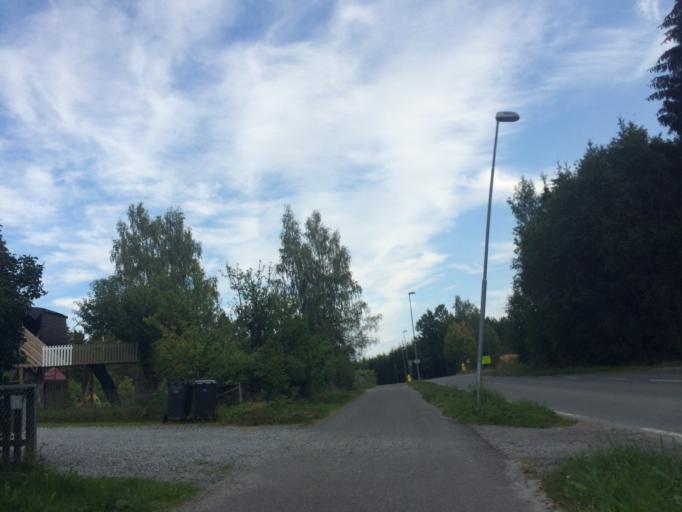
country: NO
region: Akershus
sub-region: Ski
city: Ski
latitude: 59.7005
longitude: 10.8456
